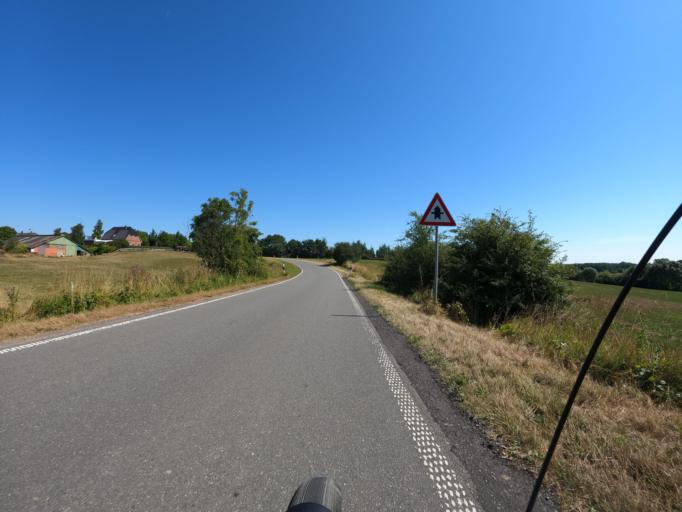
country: DE
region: Schleswig-Holstein
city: Steinberg
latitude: 54.7974
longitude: 9.7545
